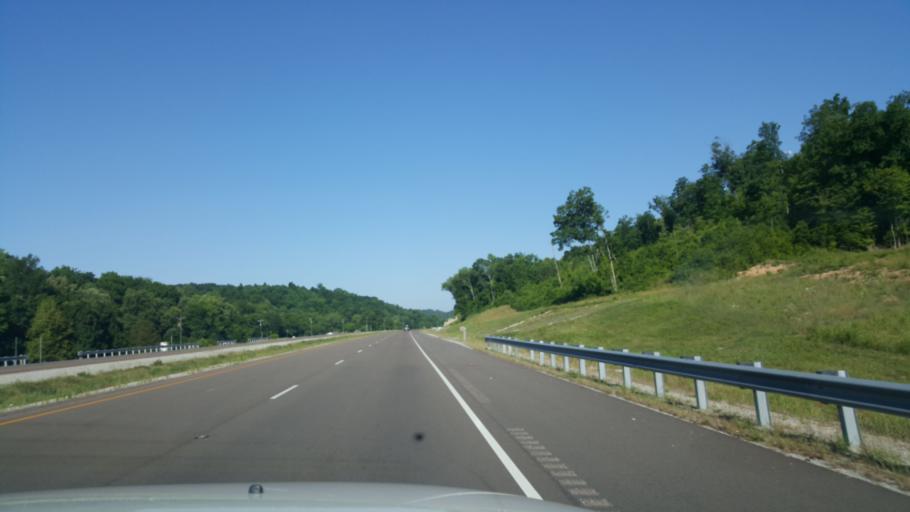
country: US
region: Tennessee
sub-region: Wayne County
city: Waynesboro
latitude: 35.2961
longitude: -87.8232
